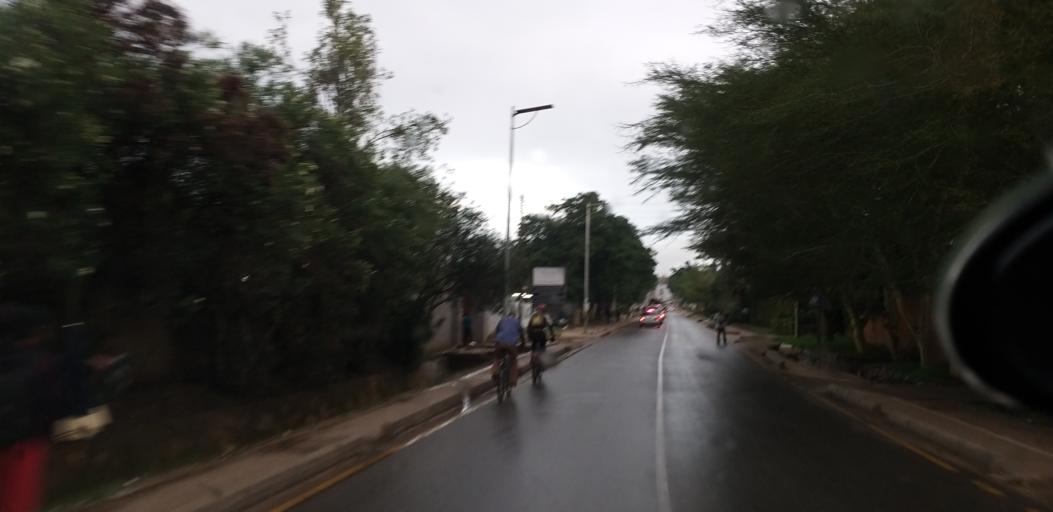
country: ZM
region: Lusaka
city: Lusaka
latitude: -15.4178
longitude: 28.3576
